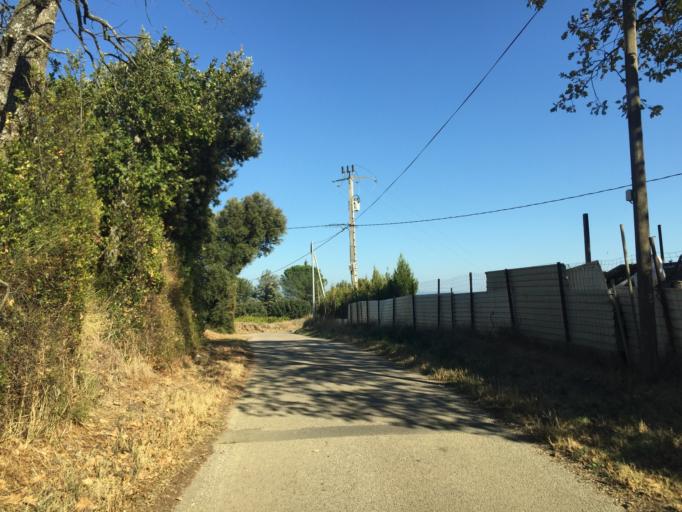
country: FR
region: Provence-Alpes-Cote d'Azur
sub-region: Departement du Vaucluse
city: Courthezon
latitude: 44.0787
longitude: 4.8665
